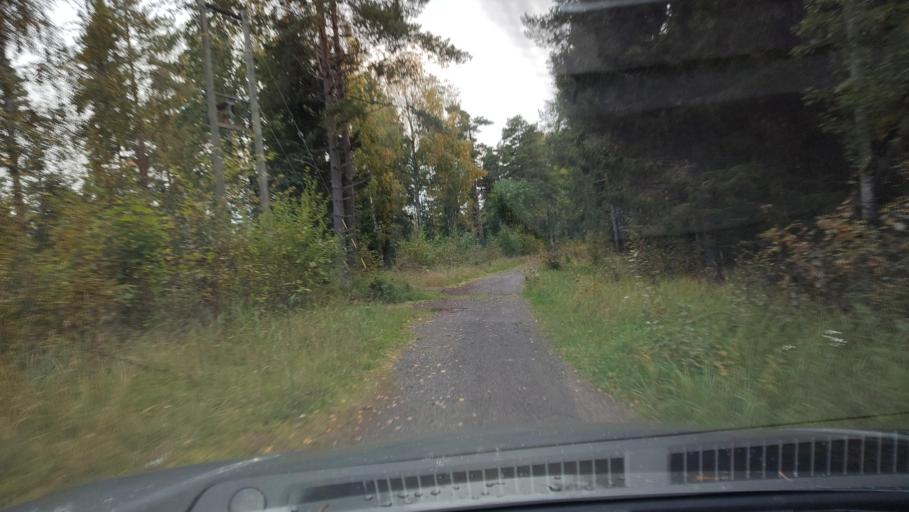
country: FI
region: Ostrobothnia
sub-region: Sydosterbotten
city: Kristinestad
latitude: 62.2675
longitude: 21.4214
